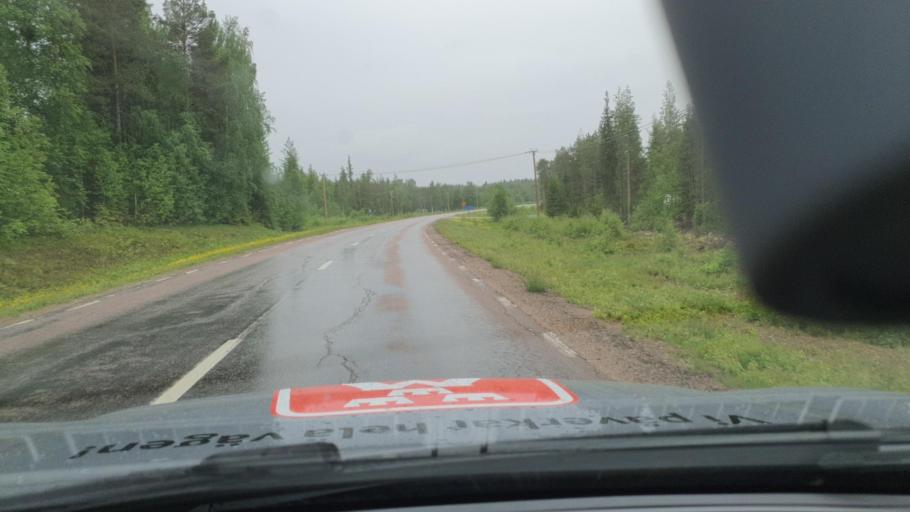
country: SE
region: Norrbotten
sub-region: Overkalix Kommun
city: OEverkalix
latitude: 66.4405
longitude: 23.2219
